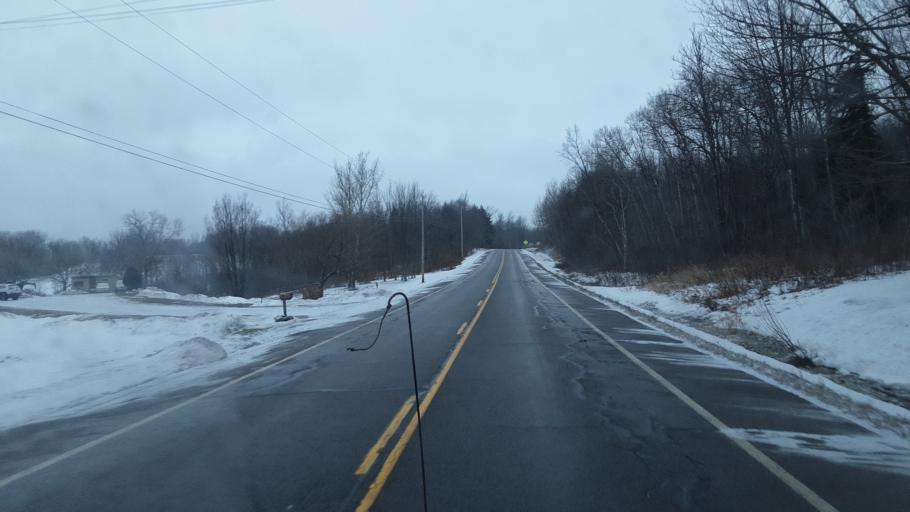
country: US
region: Pennsylvania
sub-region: Tioga County
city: Westfield
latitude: 42.0963
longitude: -77.5379
